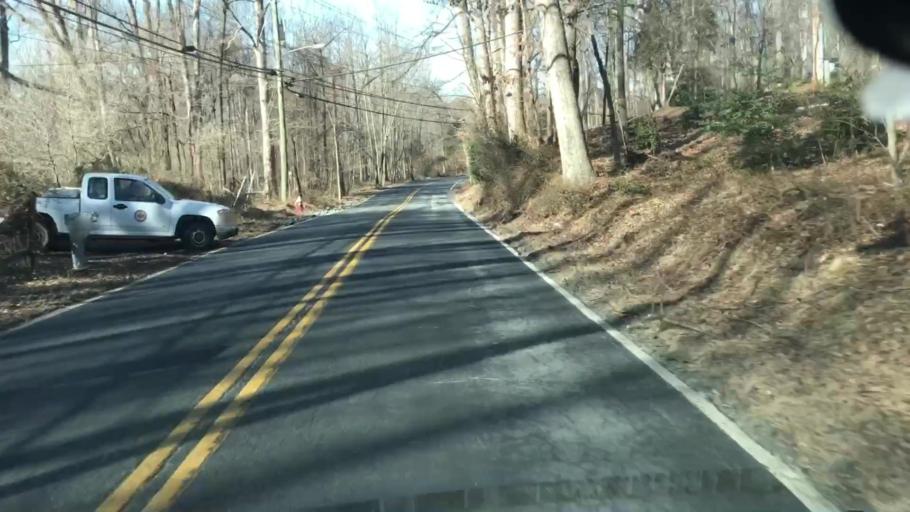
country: US
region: Virginia
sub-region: Fairfax County
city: Oakton
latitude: 38.8707
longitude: -77.3336
